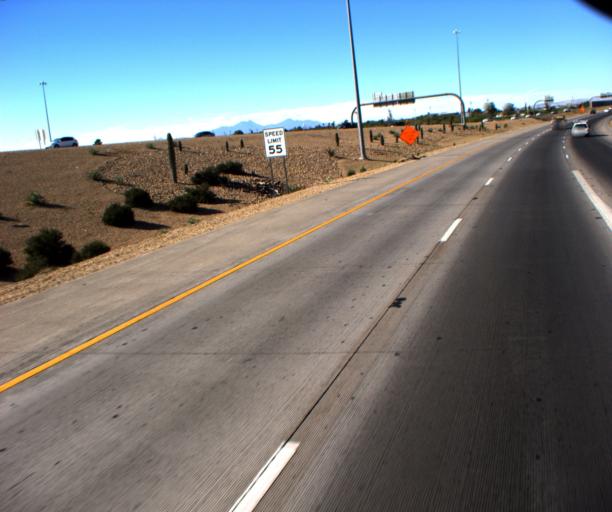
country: US
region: Arizona
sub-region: Pima County
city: South Tucson
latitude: 32.1942
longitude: -110.9795
